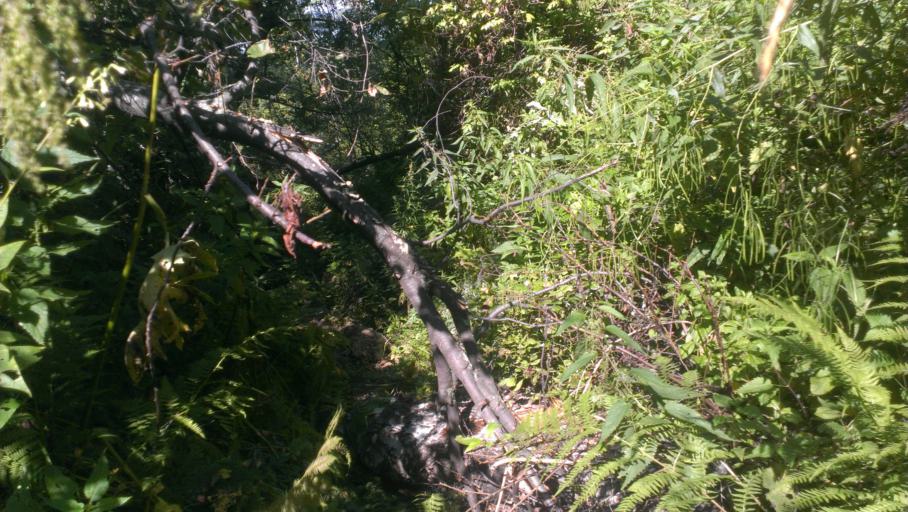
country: RU
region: Altai Krai
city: Nauchnyy Gorodok
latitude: 53.4245
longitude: 83.5047
